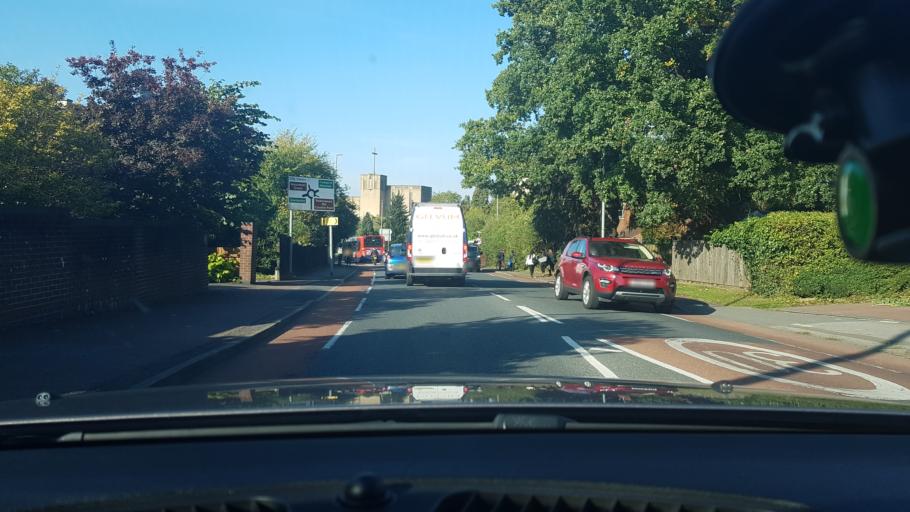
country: GB
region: England
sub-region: Gloucestershire
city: Gloucester
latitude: 51.8390
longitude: -2.2425
